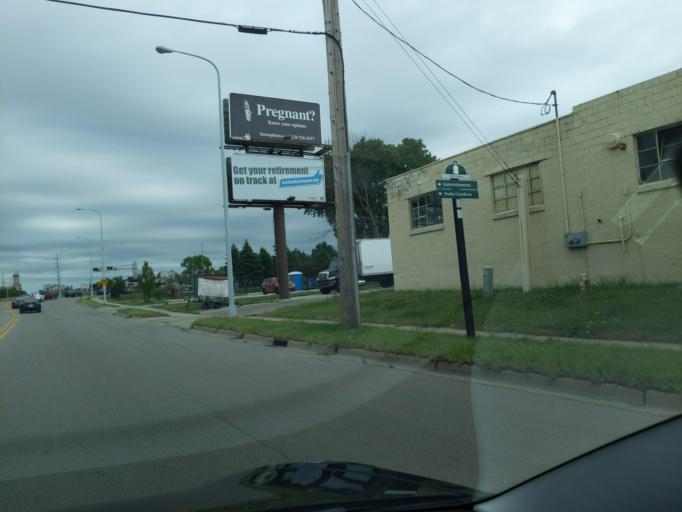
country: US
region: Michigan
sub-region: Muskegon County
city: Muskegon
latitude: 43.2293
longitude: -86.2630
